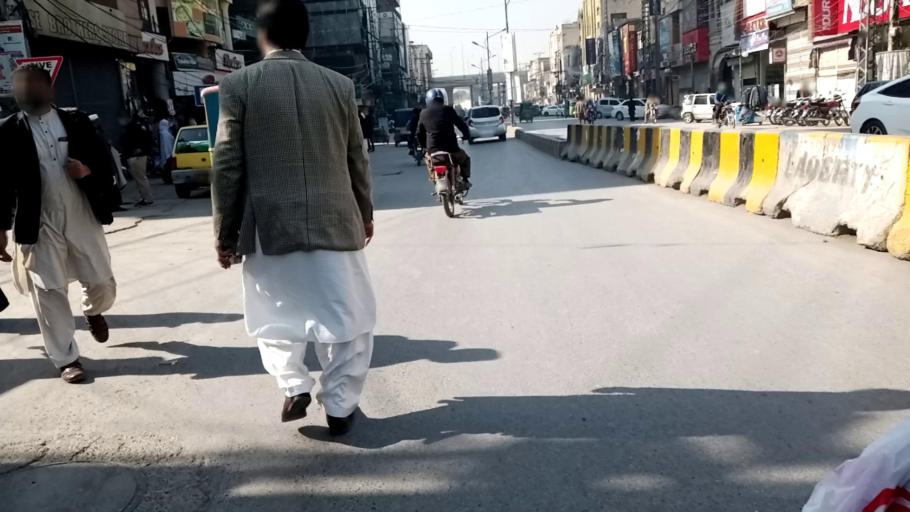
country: PK
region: Khyber Pakhtunkhwa
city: Peshawar
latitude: 33.9972
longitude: 71.5376
